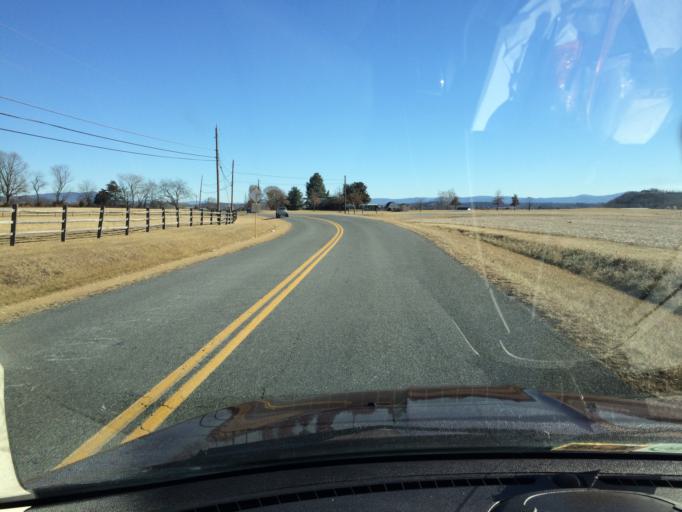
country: US
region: Virginia
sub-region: Rockingham County
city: Bridgewater
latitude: 38.3660
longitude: -78.9742
